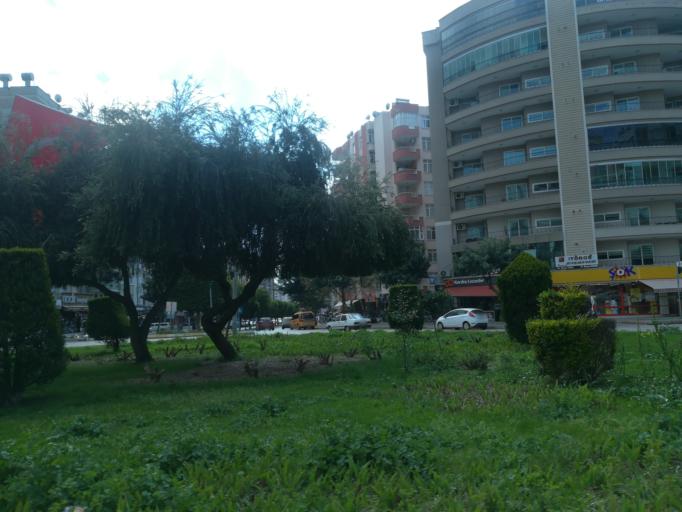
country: TR
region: Adana
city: Adana
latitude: 37.0314
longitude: 35.3005
